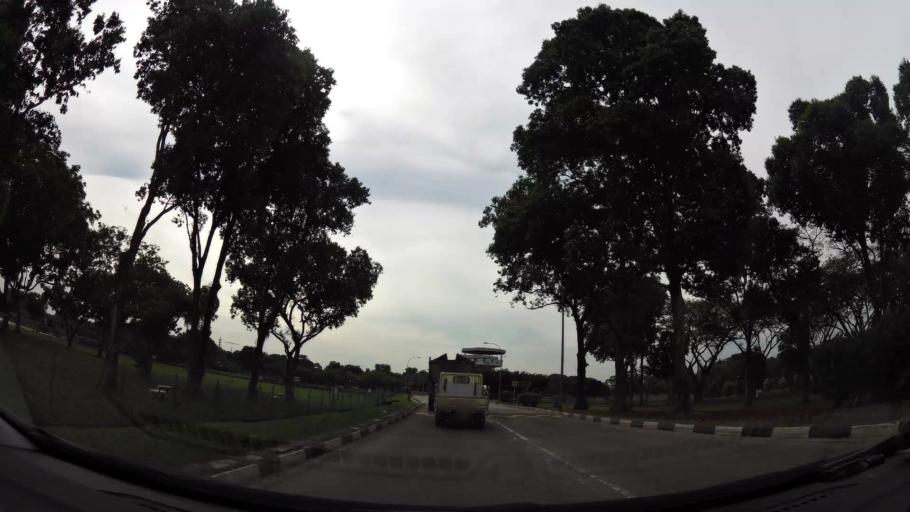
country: MY
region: Johor
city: Johor Bahru
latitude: 1.4386
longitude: 103.7379
